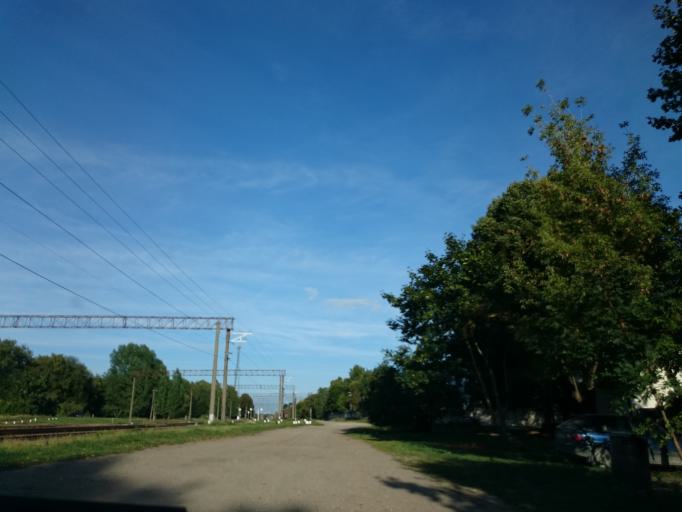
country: LV
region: Riga
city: Bergi
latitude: 56.9901
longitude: 24.2279
